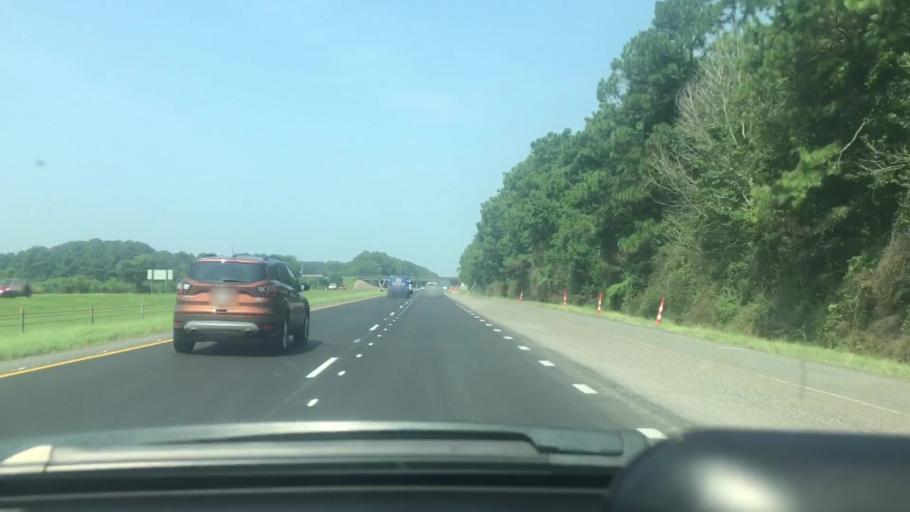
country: US
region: Louisiana
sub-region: Tangipahoa Parish
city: Hammond
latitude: 30.4792
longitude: -90.4955
